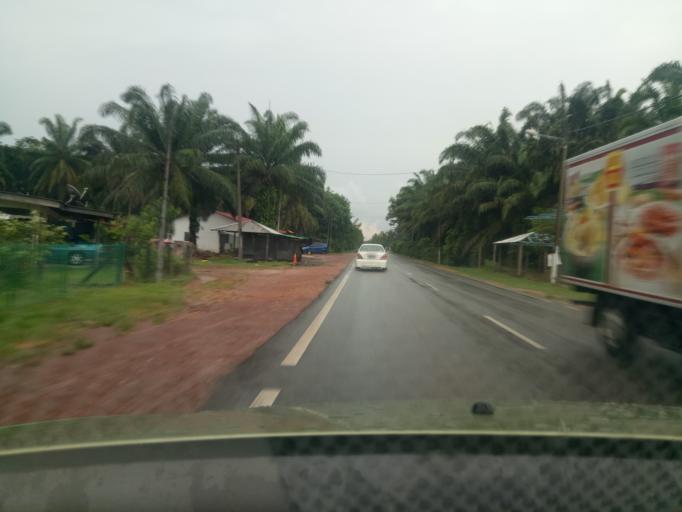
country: MY
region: Penang
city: Tasek Glugor
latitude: 5.5465
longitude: 100.5716
